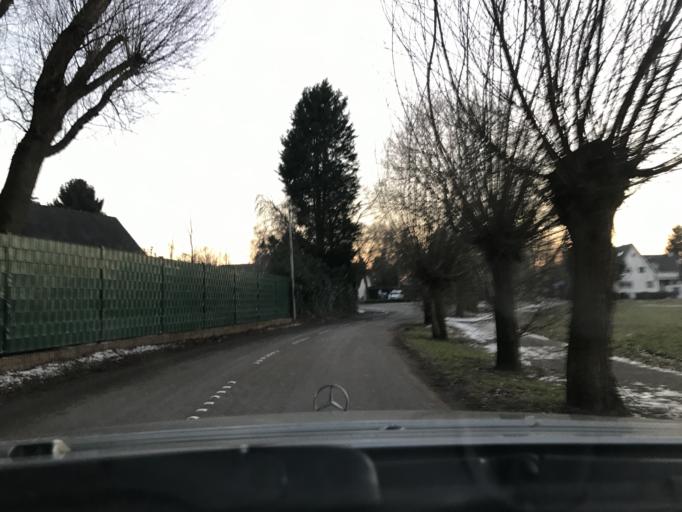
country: DE
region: North Rhine-Westphalia
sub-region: Regierungsbezirk Dusseldorf
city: Krefeld
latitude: 51.3531
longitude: 6.5542
